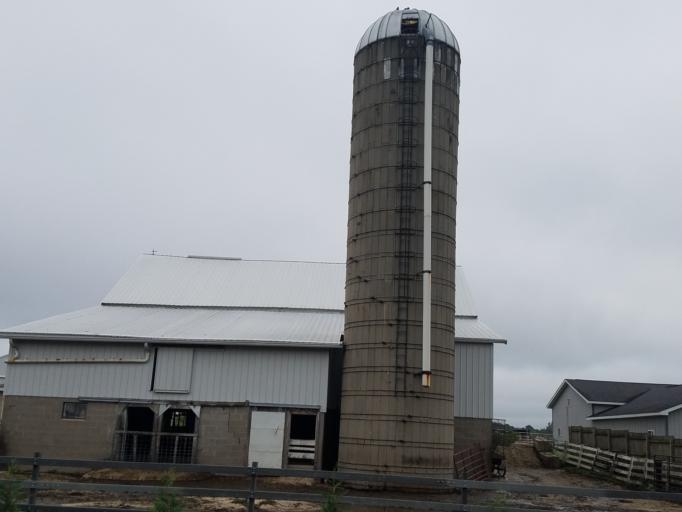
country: US
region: Indiana
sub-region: Elkhart County
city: Middlebury
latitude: 41.6771
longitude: -85.5687
